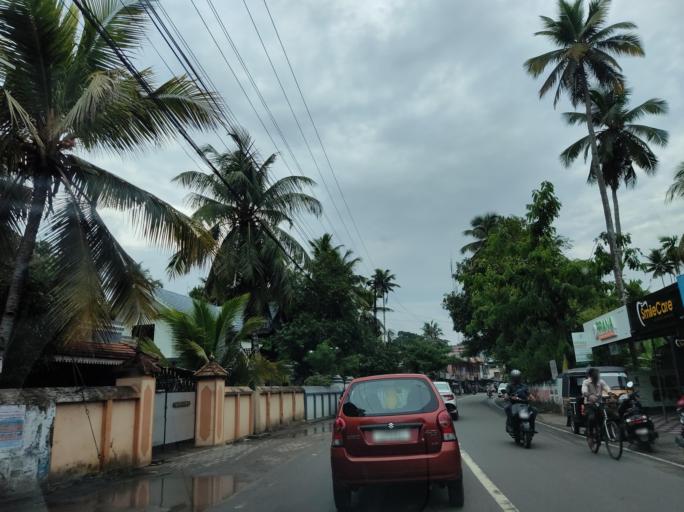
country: IN
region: Kerala
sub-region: Alappuzha
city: Mavelikara
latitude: 9.2510
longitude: 76.4892
